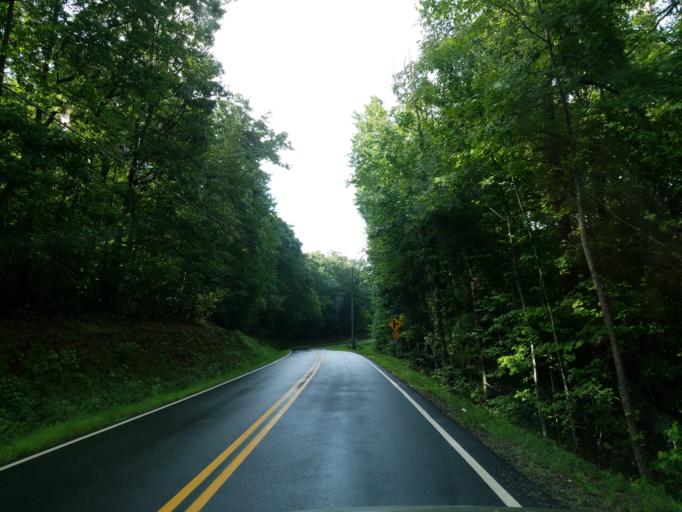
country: US
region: Georgia
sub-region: White County
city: Cleveland
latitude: 34.6298
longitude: -83.8673
